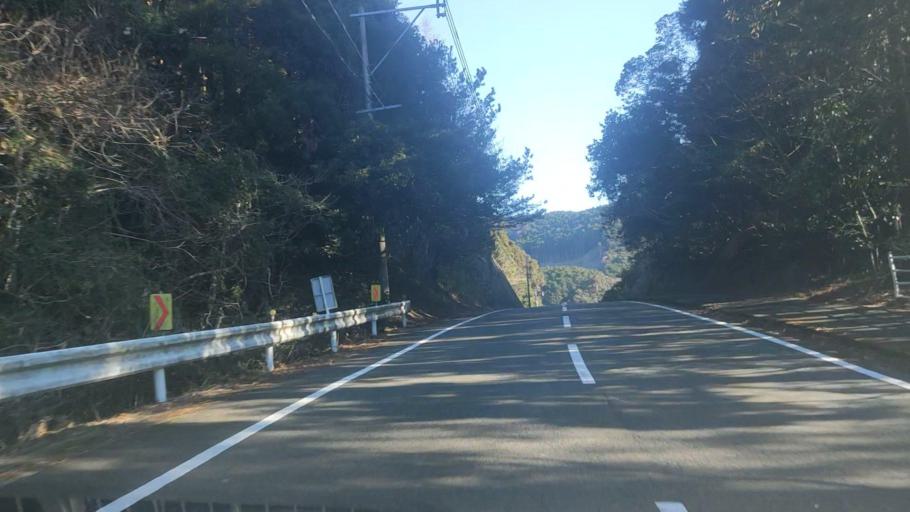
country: JP
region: Miyazaki
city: Nobeoka
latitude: 32.6869
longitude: 131.8044
